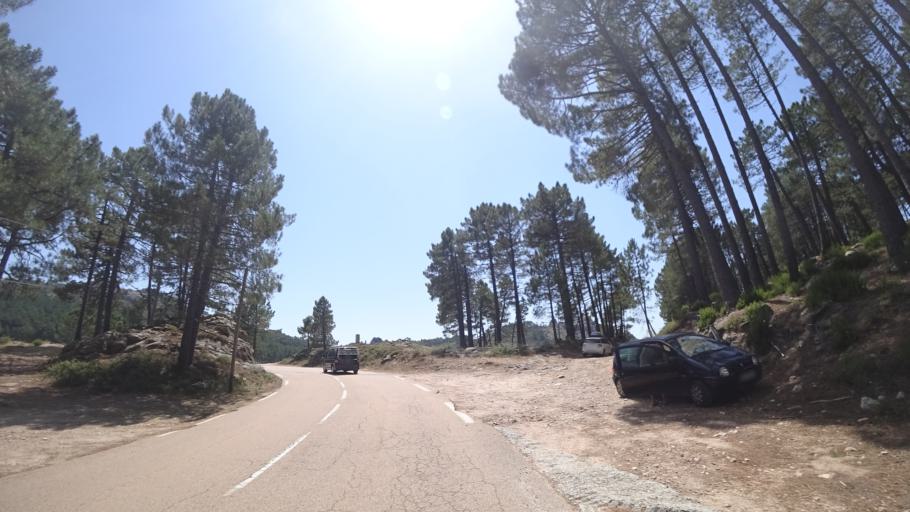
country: FR
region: Corsica
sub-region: Departement de la Corse-du-Sud
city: Zonza
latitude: 41.6694
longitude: 9.2064
